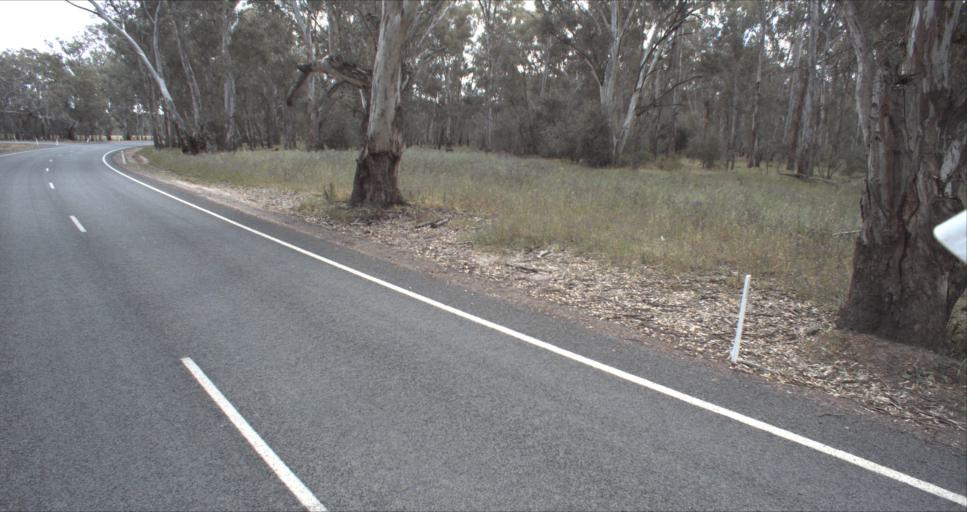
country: AU
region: New South Wales
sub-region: Leeton
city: Leeton
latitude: -34.6409
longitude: 146.3691
